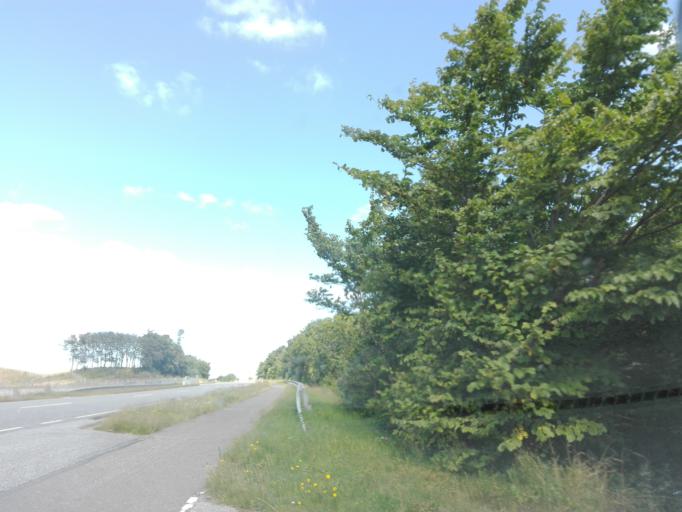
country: DK
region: Central Jutland
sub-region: Randers Kommune
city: Randers
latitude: 56.4033
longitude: 10.0836
